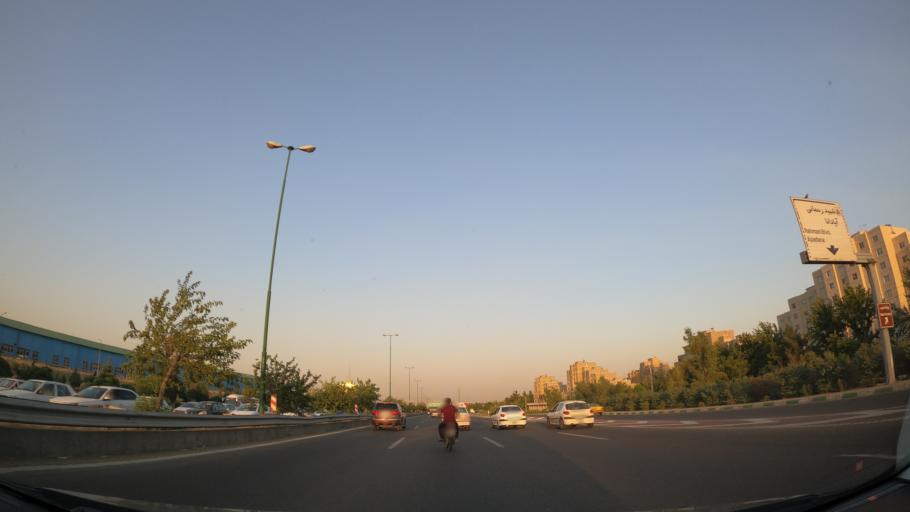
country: IR
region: Tehran
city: Tehran
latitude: 35.7146
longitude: 51.3242
